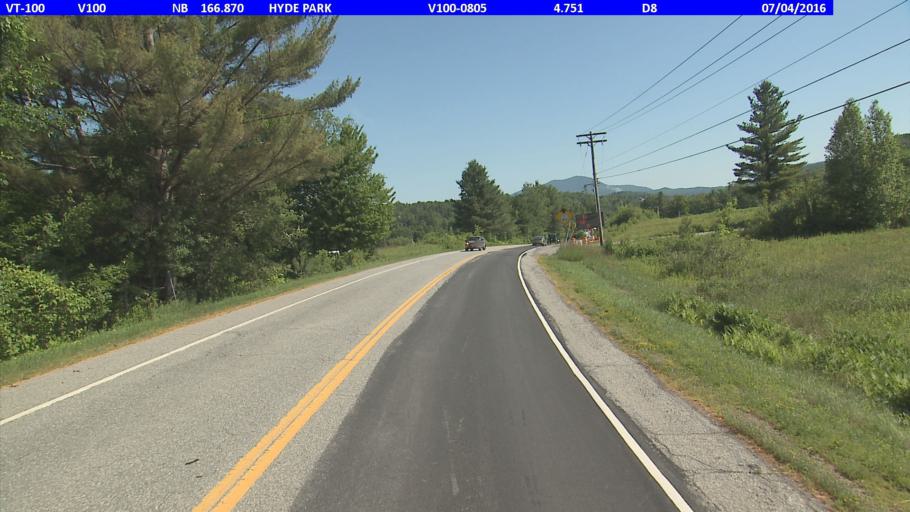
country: US
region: Vermont
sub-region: Lamoille County
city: Hyde Park
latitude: 44.6615
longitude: -72.6069
